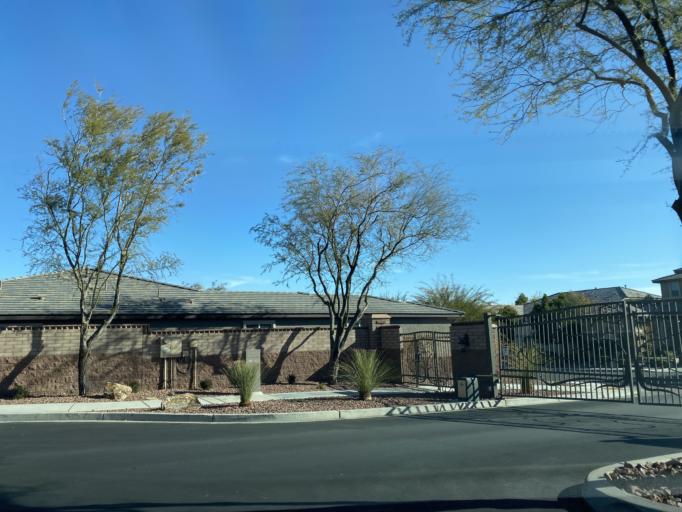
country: US
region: Nevada
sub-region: Clark County
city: Summerlin South
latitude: 36.2880
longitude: -115.3219
